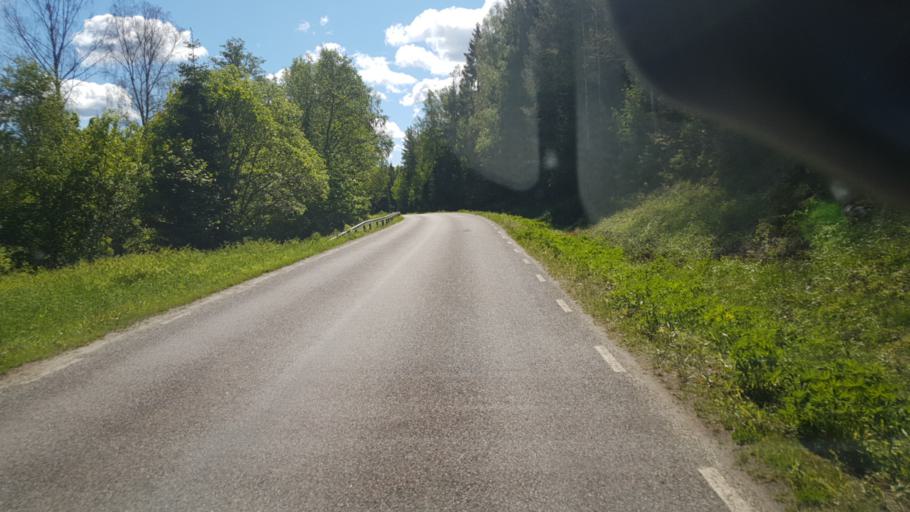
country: SE
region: Vaermland
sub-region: Grums Kommun
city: Grums
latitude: 59.5107
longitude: 12.8651
